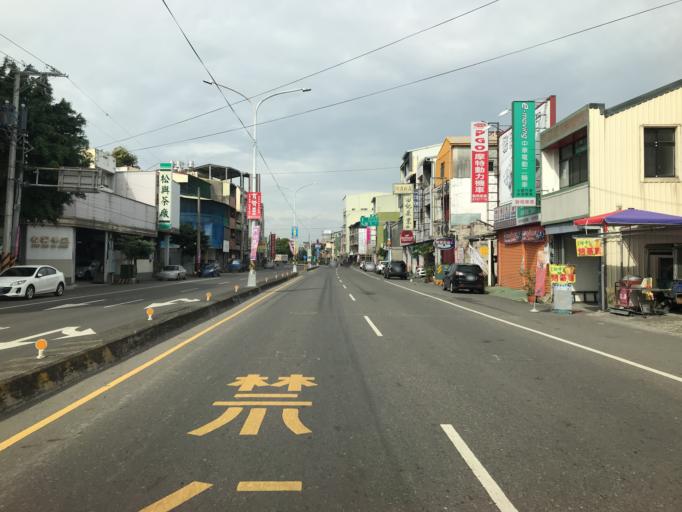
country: TW
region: Taiwan
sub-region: Nantou
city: Nantou
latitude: 23.8532
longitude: 120.5889
